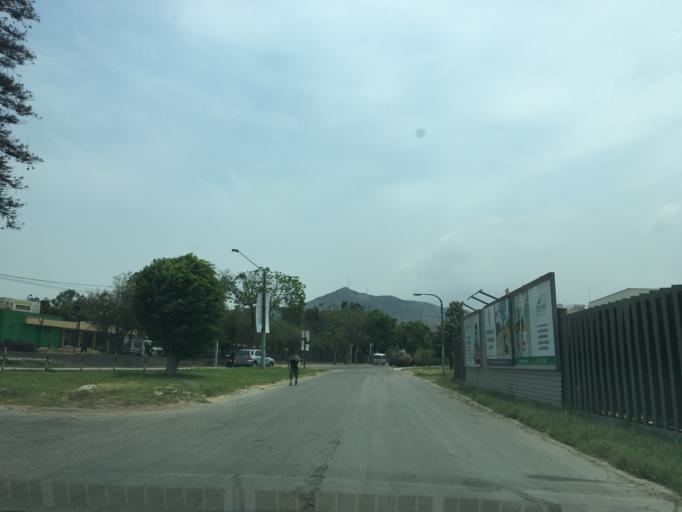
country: PE
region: Lima
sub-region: Lima
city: La Molina
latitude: -12.0798
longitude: -76.9509
